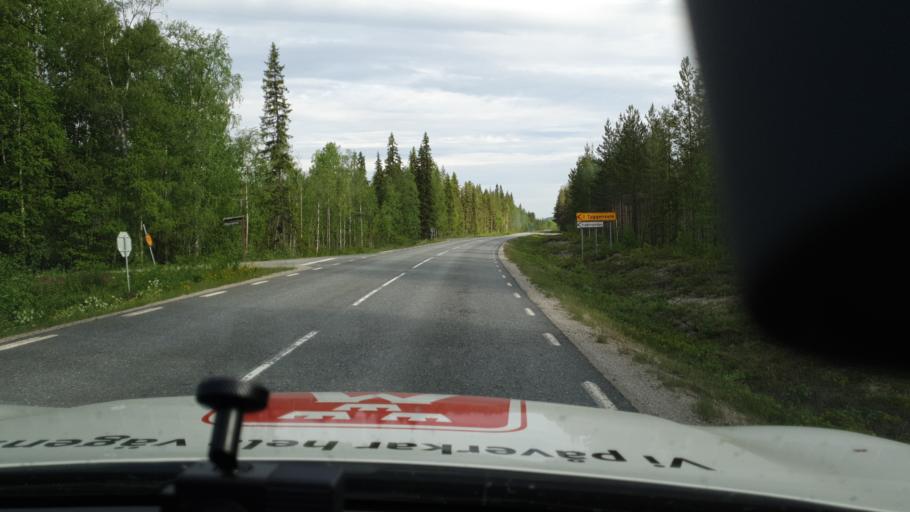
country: SE
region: Vaesterbotten
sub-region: Lycksele Kommun
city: Lycksele
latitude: 64.4589
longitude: 18.9051
